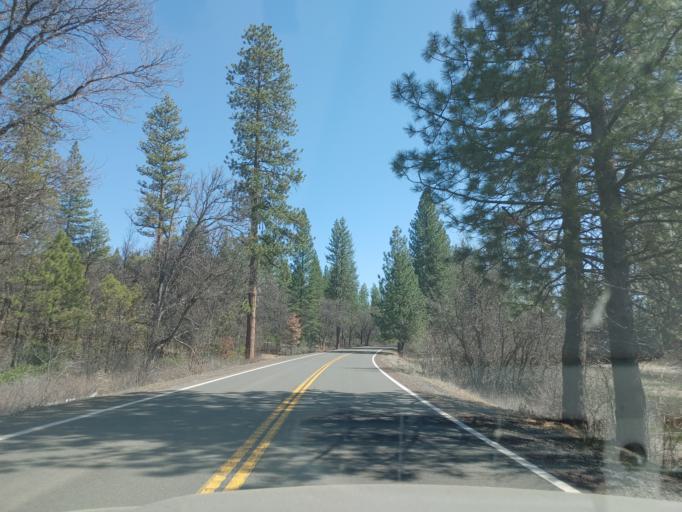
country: US
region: California
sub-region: Shasta County
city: Burney
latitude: 41.0062
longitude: -121.6338
